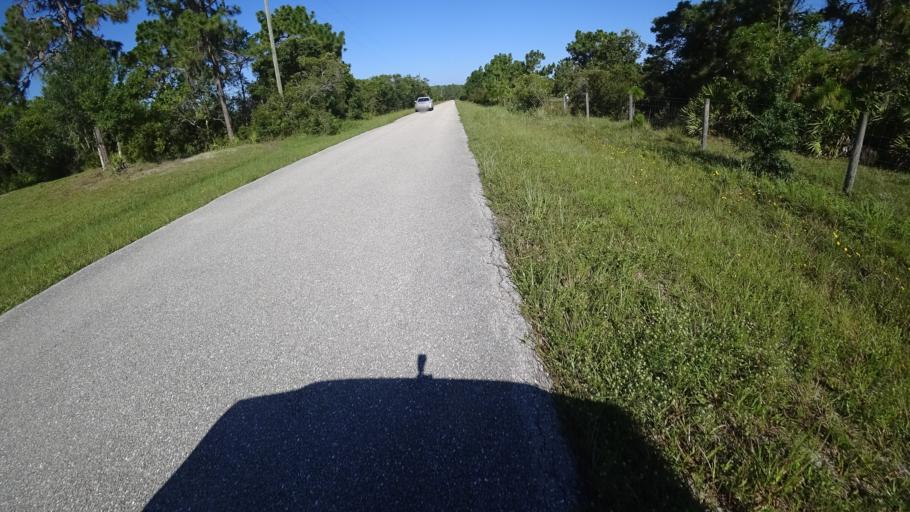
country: US
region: Florida
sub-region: Sarasota County
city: The Meadows
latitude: 27.4129
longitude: -82.3138
